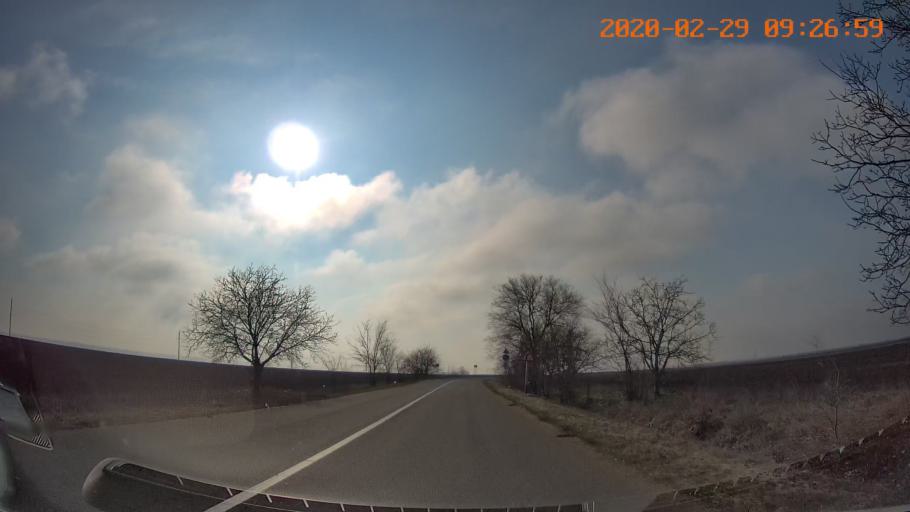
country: MD
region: Telenesti
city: Pervomaisc
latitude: 46.7003
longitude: 29.9460
